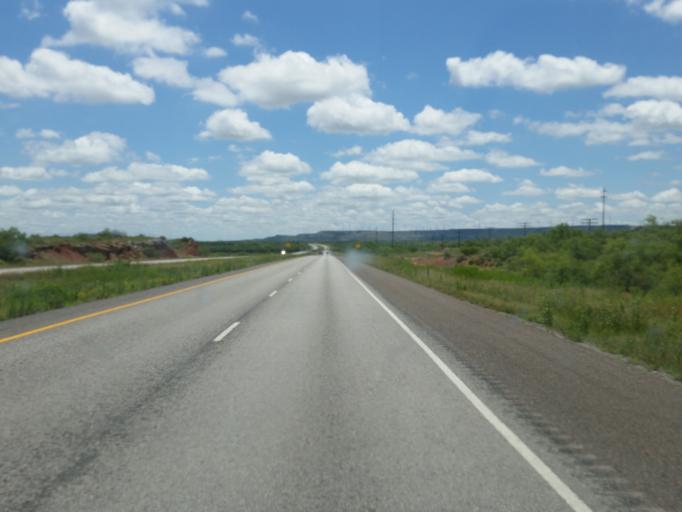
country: US
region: Texas
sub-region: Garza County
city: Post
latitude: 33.0122
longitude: -101.1742
